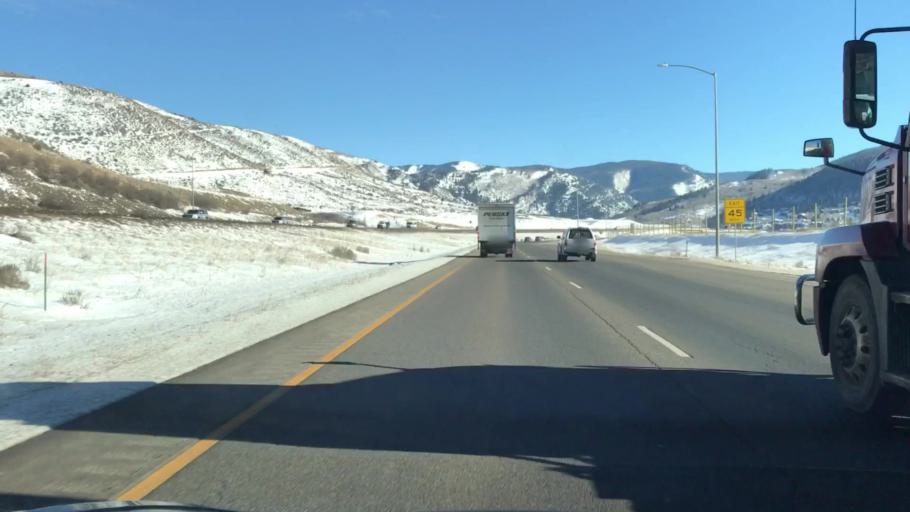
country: US
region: Colorado
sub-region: Eagle County
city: Avon
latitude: 39.6300
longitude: -106.5007
